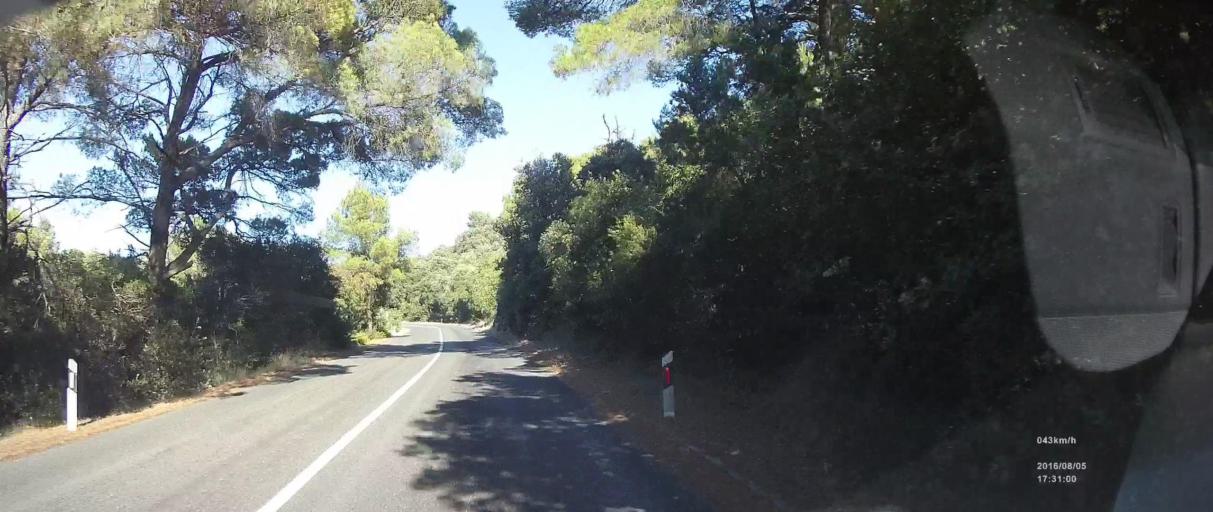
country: HR
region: Dubrovacko-Neretvanska
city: Blato
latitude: 42.7737
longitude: 17.4164
